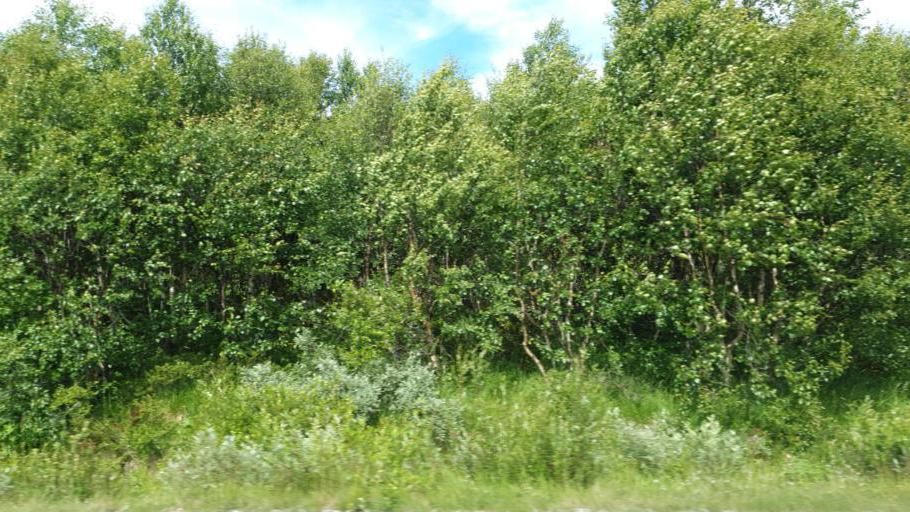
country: NO
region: Oppland
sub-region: Oystre Slidre
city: Heggenes
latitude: 61.5159
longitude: 8.8583
